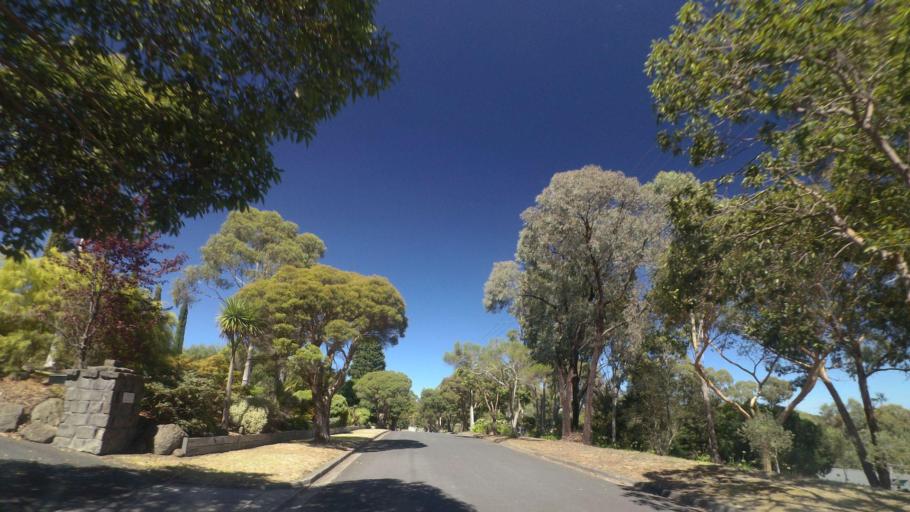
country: AU
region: Victoria
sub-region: Manningham
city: Donvale
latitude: -37.7945
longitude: 145.1922
